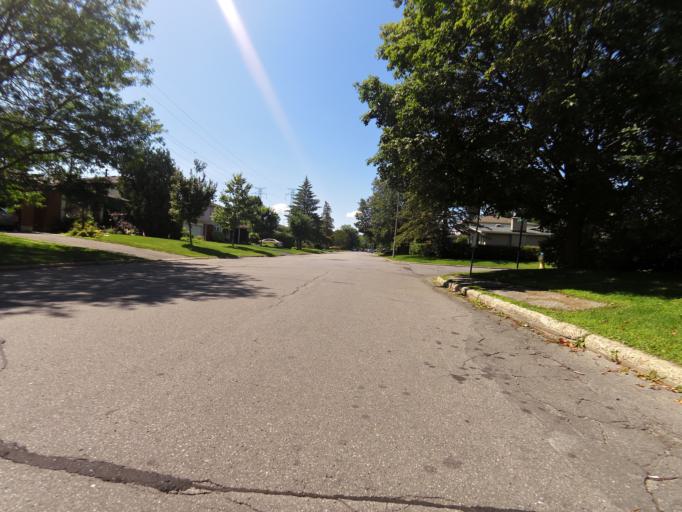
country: CA
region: Ontario
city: Ottawa
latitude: 45.3597
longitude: -75.6769
